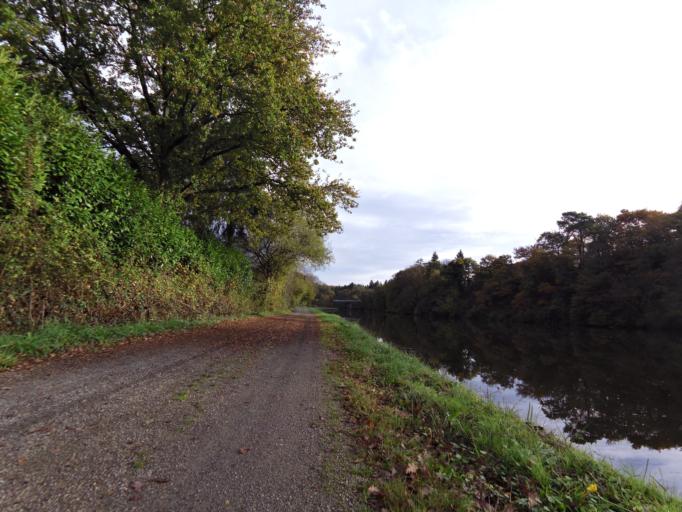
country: FR
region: Brittany
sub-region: Departement d'Ille-et-Vilaine
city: Bourg-des-Comptes
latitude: 47.9340
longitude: -1.7579
